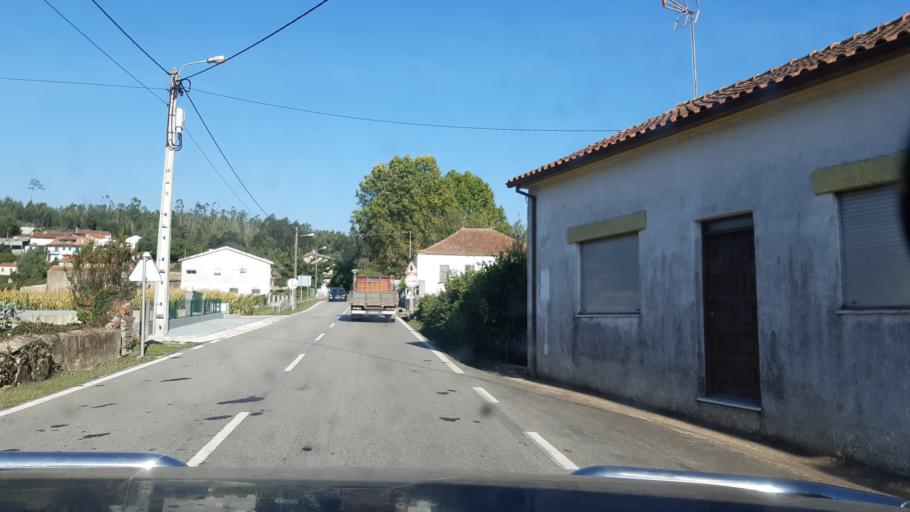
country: PT
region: Aveiro
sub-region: Agueda
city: Agueda
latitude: 40.5636
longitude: -8.3965
